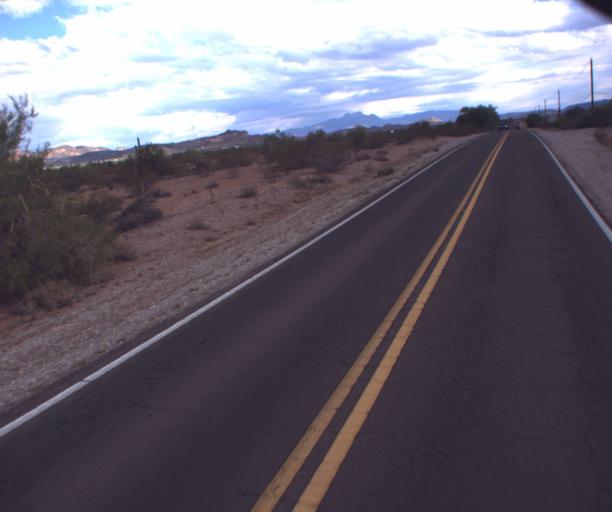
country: US
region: Arizona
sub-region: Pinal County
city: Apache Junction
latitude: 33.4240
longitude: -111.5393
